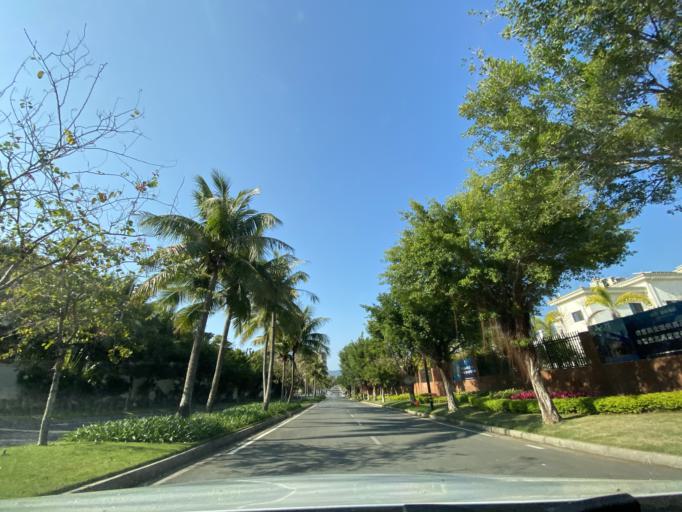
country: CN
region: Hainan
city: Yingzhou
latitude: 18.4165
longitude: 109.8889
